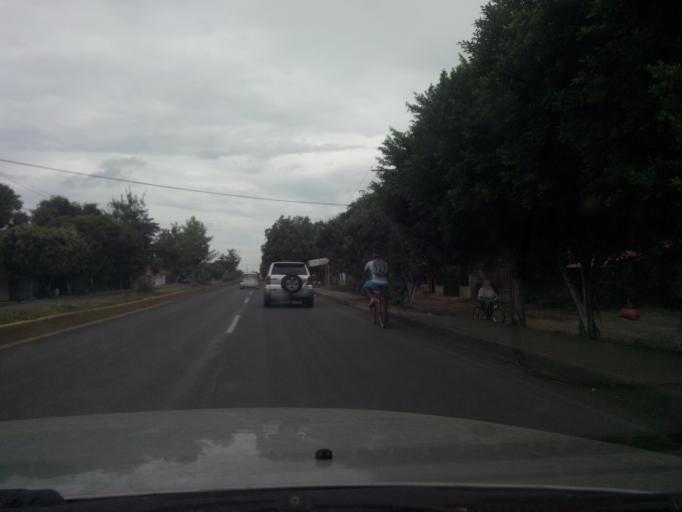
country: NI
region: Masaya
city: Masaya
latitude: 11.9852
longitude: -86.0921
